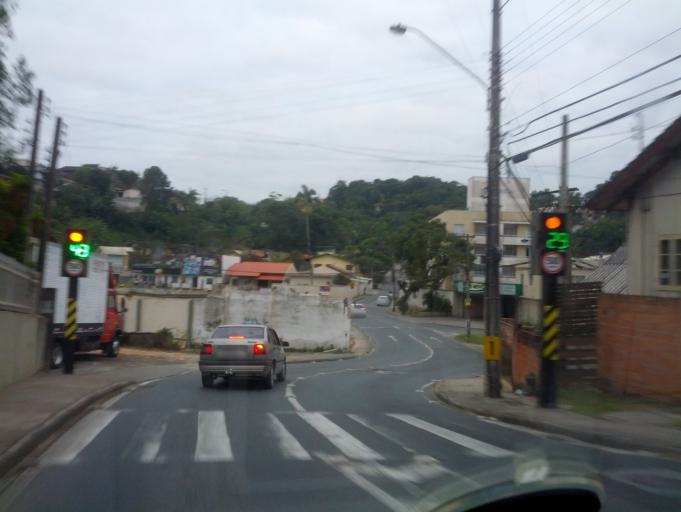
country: BR
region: Santa Catarina
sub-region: Blumenau
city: Blumenau
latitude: -26.8764
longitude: -49.0815
